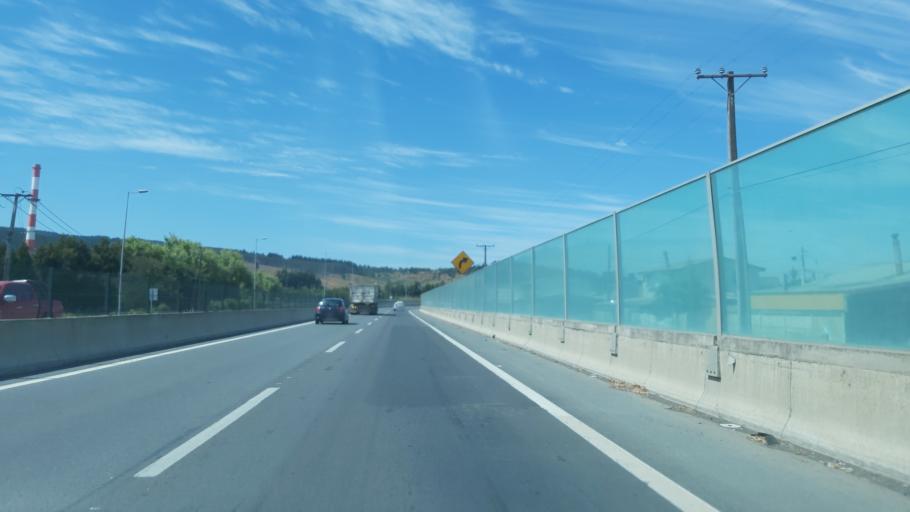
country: CL
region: Biobio
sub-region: Provincia de Concepcion
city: Coronel
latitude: -37.0366
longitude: -73.1349
